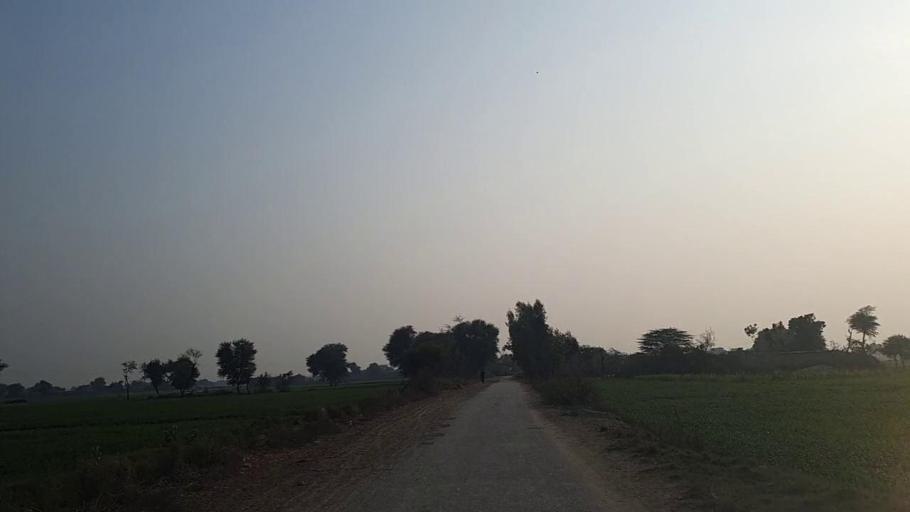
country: PK
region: Sindh
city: Nawabshah
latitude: 26.2138
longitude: 68.4723
